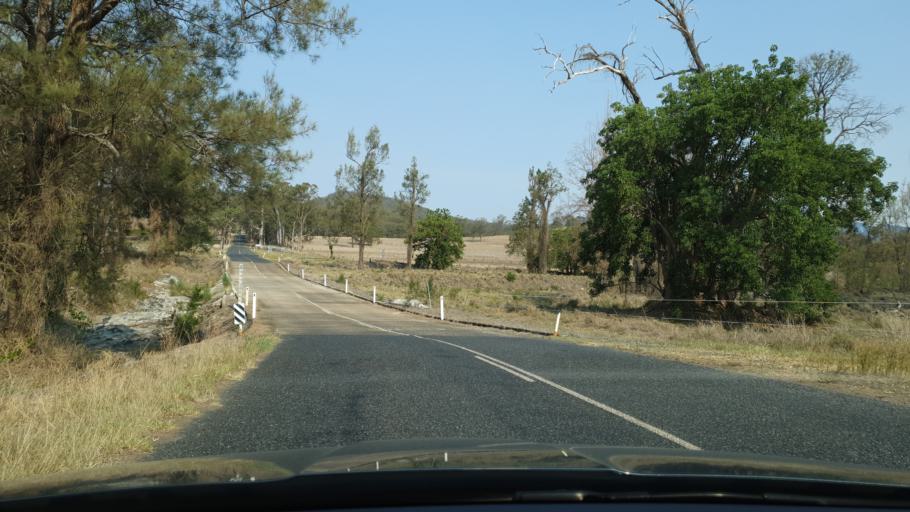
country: AU
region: Queensland
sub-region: Southern Downs
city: Warwick
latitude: -28.1823
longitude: 152.5447
